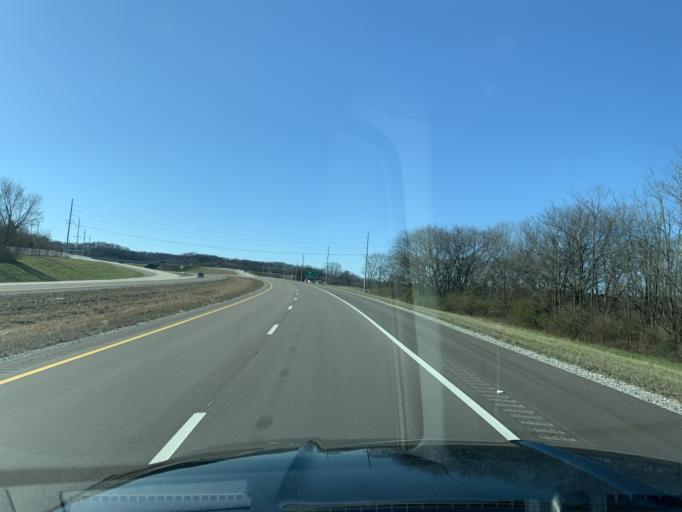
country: US
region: Tennessee
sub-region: Maury County
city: Mount Pleasant
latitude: 35.5490
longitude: -87.2169
